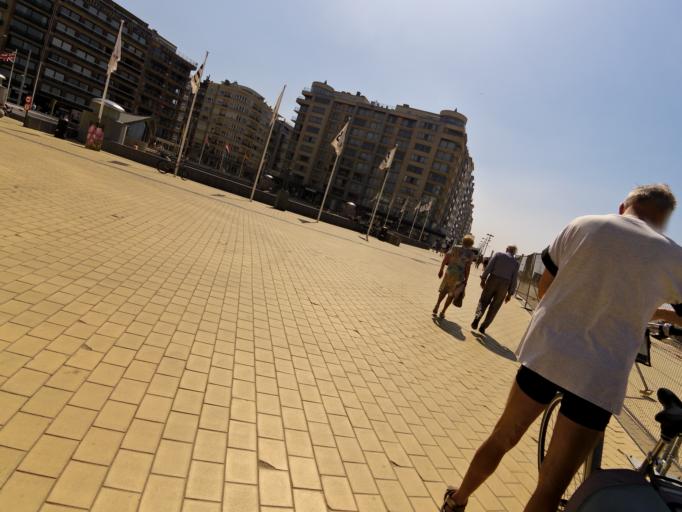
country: BE
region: Flanders
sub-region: Provincie West-Vlaanderen
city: Middelkerke
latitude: 51.1878
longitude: 2.8139
